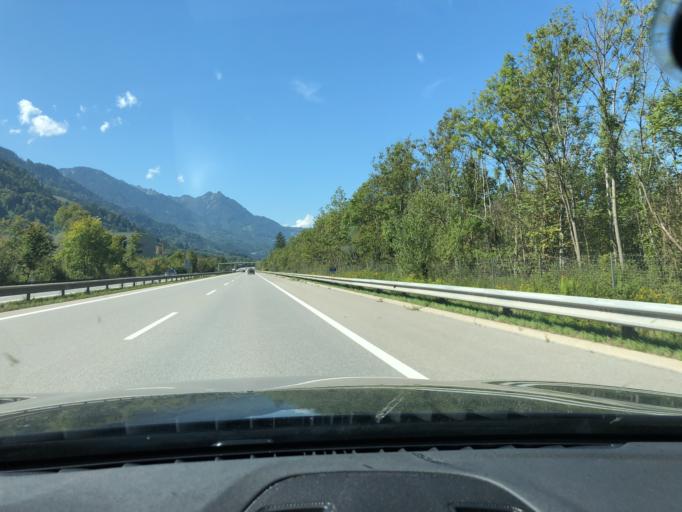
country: AT
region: Vorarlberg
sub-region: Politischer Bezirk Bludenz
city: Thuringen
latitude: 47.1752
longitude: 9.7555
